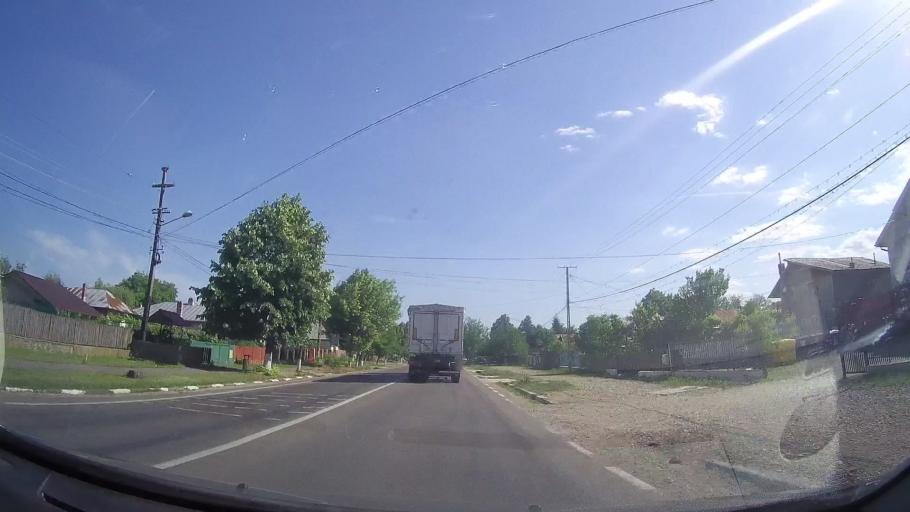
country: RO
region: Prahova
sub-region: Comuna Lipanesti
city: Lipanesti
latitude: 45.0553
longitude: 26.0202
